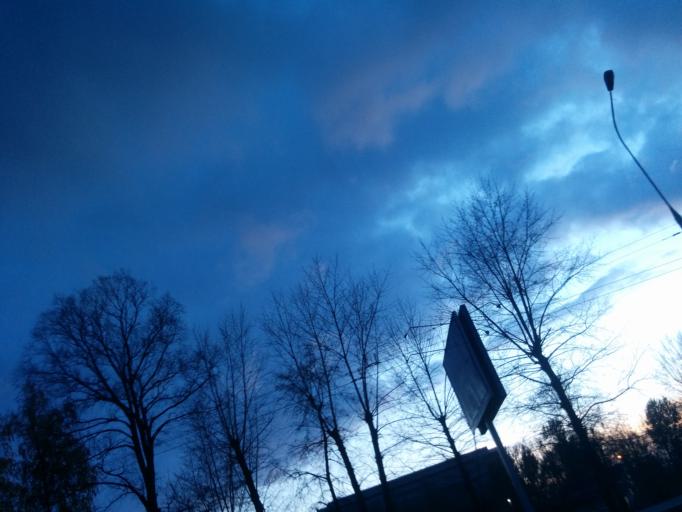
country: RU
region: Moscow
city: Nagornyy
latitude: 55.6587
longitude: 37.6409
